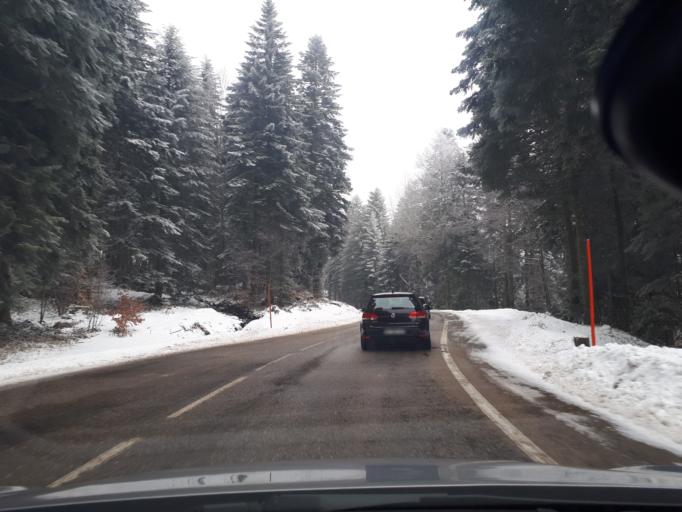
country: FR
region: Rhone-Alpes
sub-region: Departement de l'Isere
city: Vaulnaveys-le-Bas
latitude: 45.1011
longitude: 5.8494
